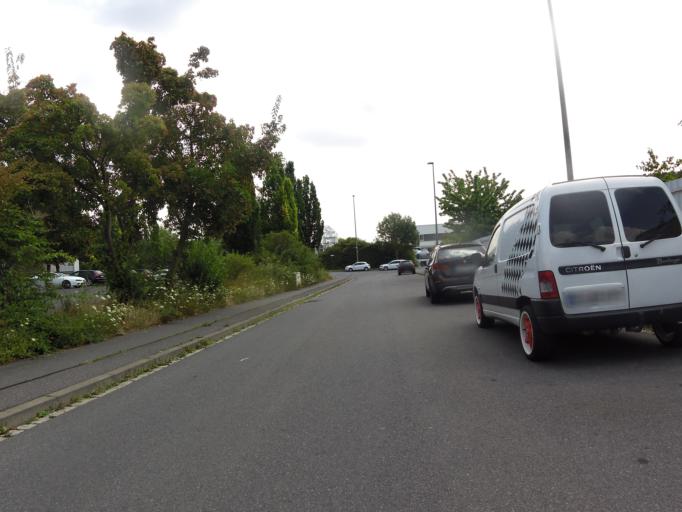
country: DE
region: Bavaria
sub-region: Regierungsbezirk Unterfranken
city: Eibelstadt
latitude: 49.7311
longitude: 9.9677
